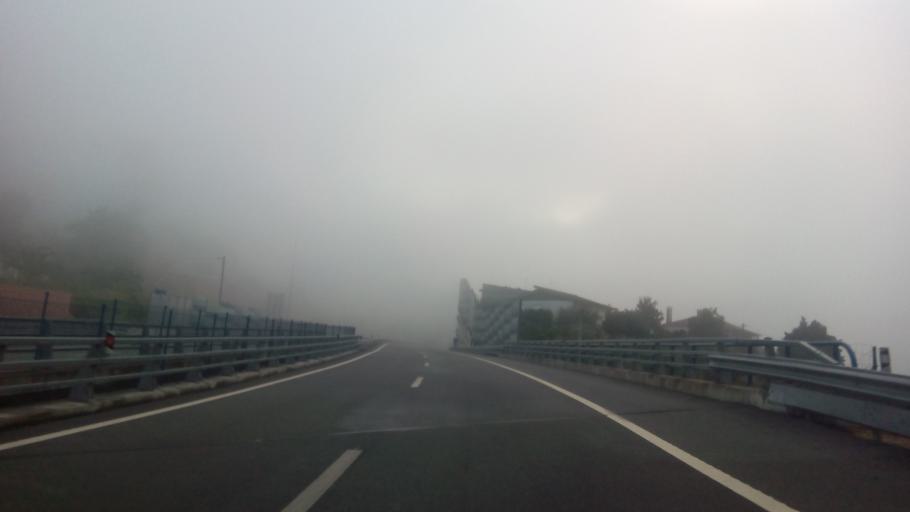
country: PT
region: Porto
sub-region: Amarante
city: Amarante
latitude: 41.2587
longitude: -8.0594
